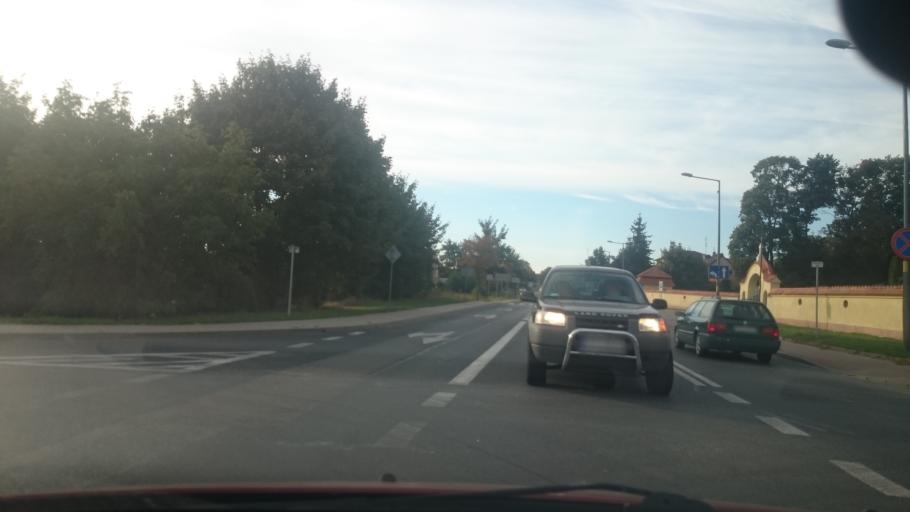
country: PL
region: Lower Silesian Voivodeship
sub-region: Powiat trzebnicki
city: Trzebnica
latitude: 51.3176
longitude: 17.0610
